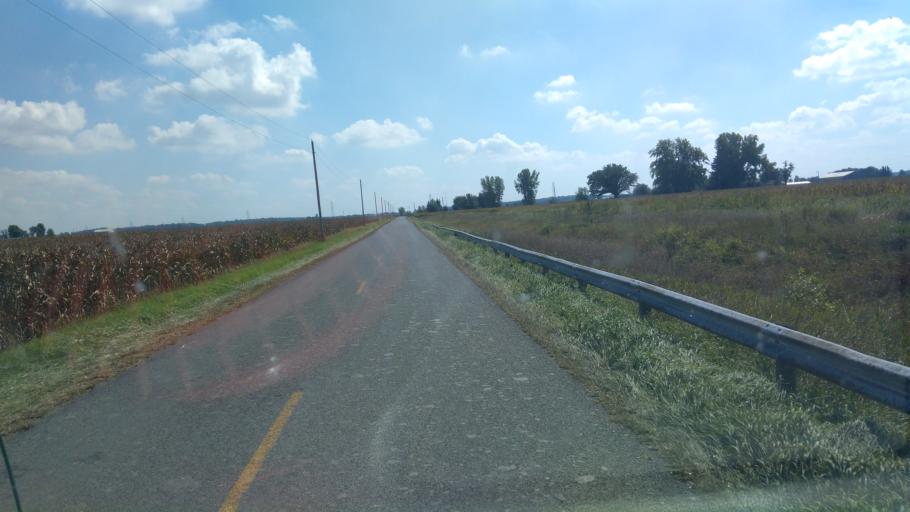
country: US
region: Ohio
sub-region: Hardin County
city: Ada
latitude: 40.6813
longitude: -83.8421
